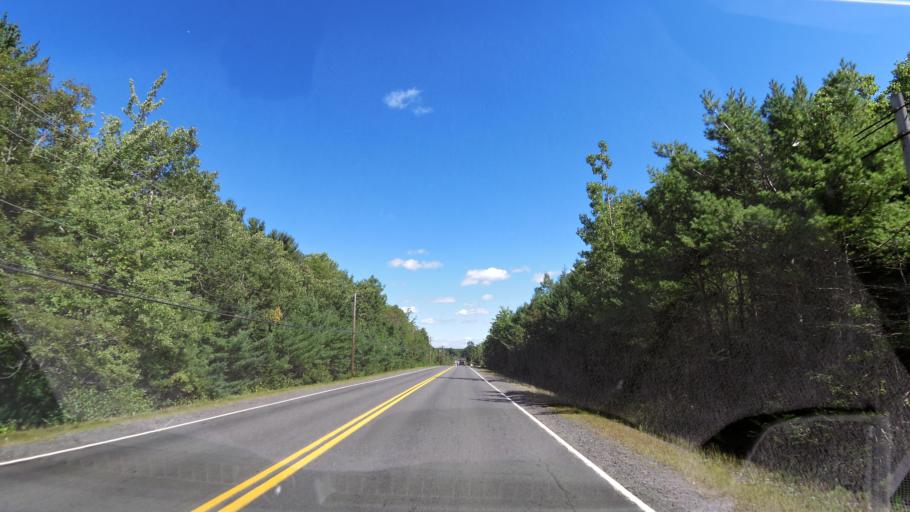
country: CA
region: Nova Scotia
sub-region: Kings County
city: Kentville
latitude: 45.0598
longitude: -64.6071
